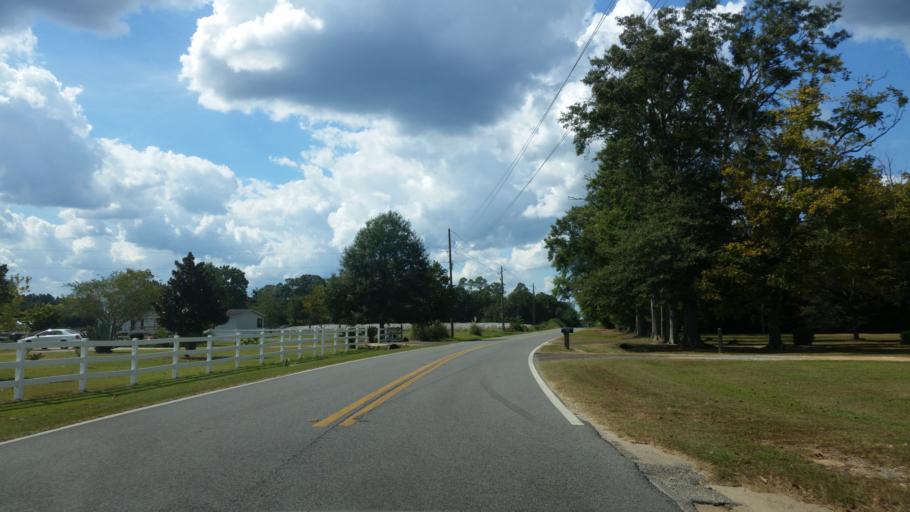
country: US
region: Alabama
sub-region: Escambia County
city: Atmore
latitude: 30.8855
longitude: -87.5074
